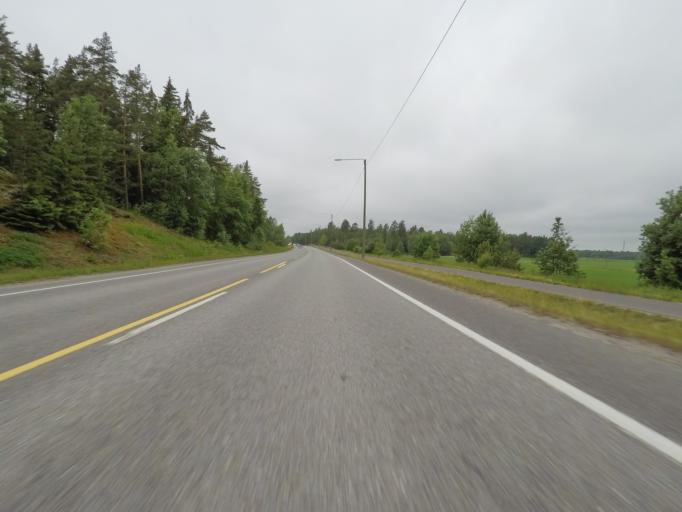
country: FI
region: Varsinais-Suomi
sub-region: Turku
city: Naantali
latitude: 60.4684
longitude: 22.0913
